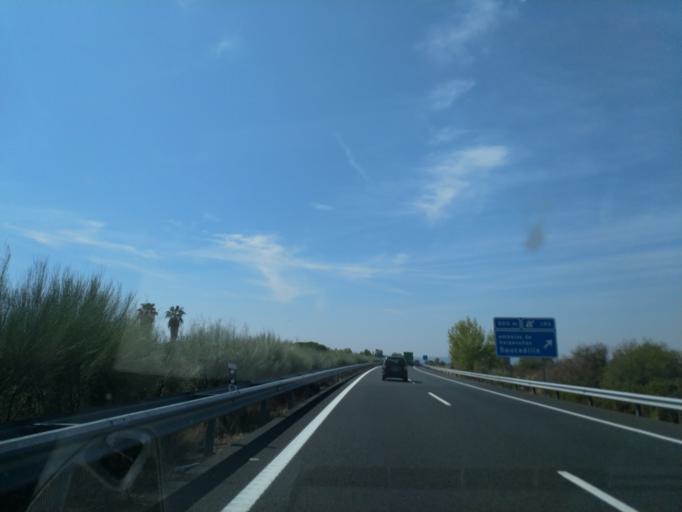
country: ES
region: Extremadura
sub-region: Provincia de Caceres
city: Millanes
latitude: 39.8557
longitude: -5.6178
